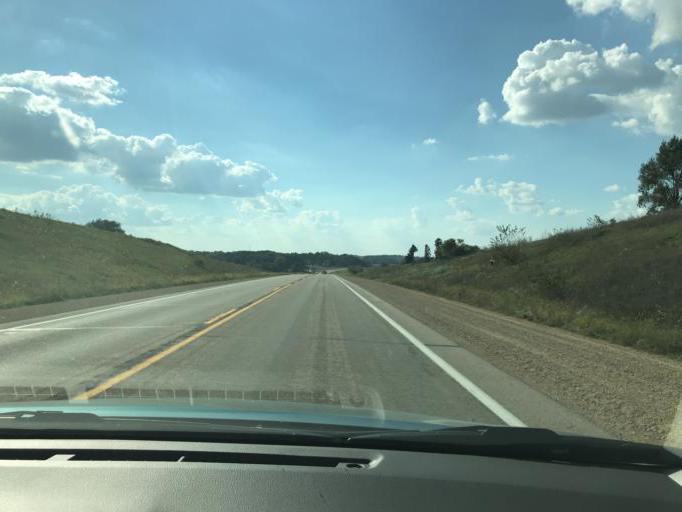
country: US
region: Wisconsin
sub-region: Green County
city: Brodhead
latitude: 42.5885
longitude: -89.4731
